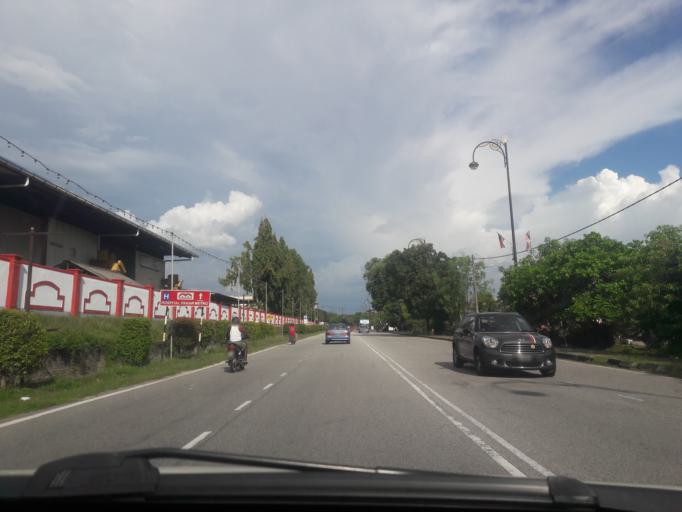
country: MY
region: Kedah
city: Sungai Petani
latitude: 5.6523
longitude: 100.5020
